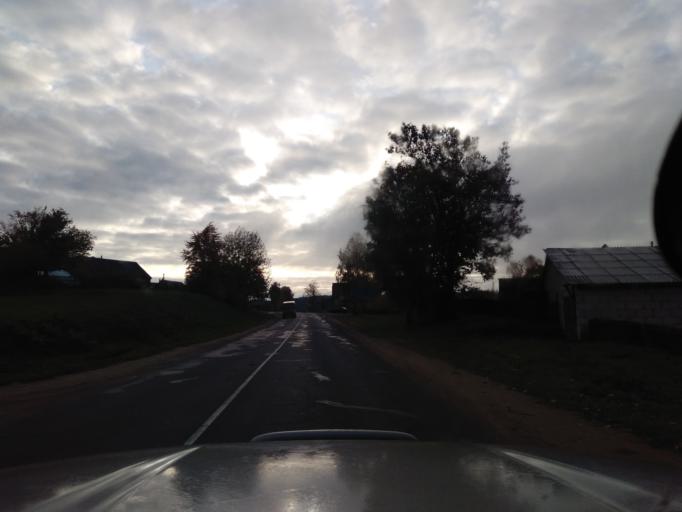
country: BY
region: Minsk
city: Kapyl'
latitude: 53.1600
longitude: 27.0912
